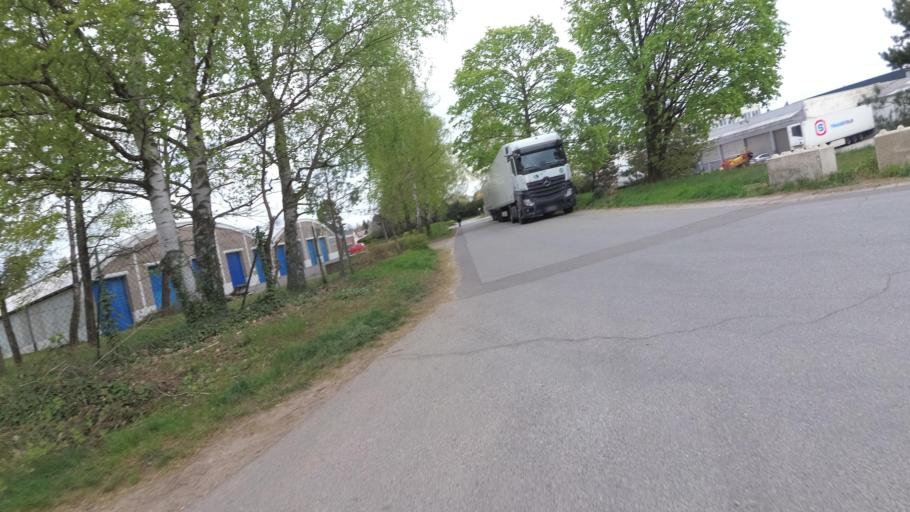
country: DE
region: Saarland
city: Bexbach
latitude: 49.3071
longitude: 7.2869
